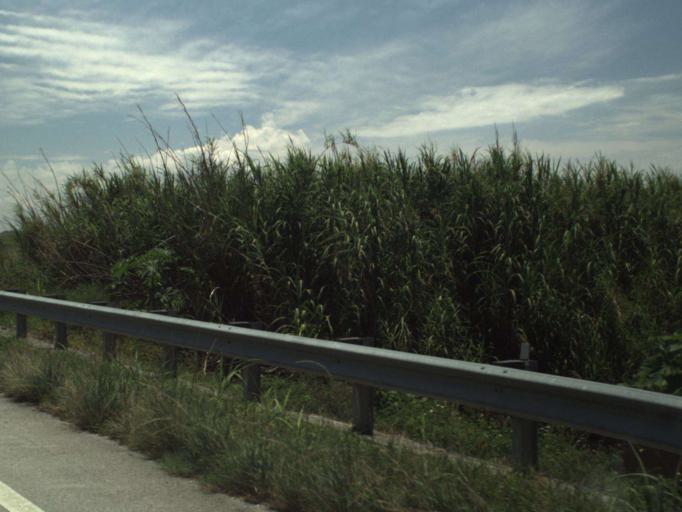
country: US
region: Florida
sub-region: Martin County
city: Indiantown
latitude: 26.9660
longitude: -80.6106
